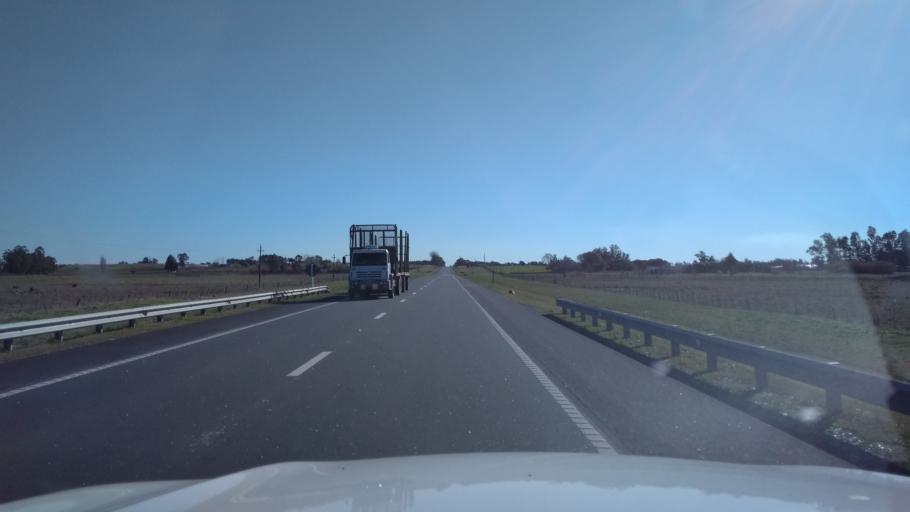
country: UY
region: Canelones
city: San Jacinto
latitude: -34.5272
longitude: -55.9575
